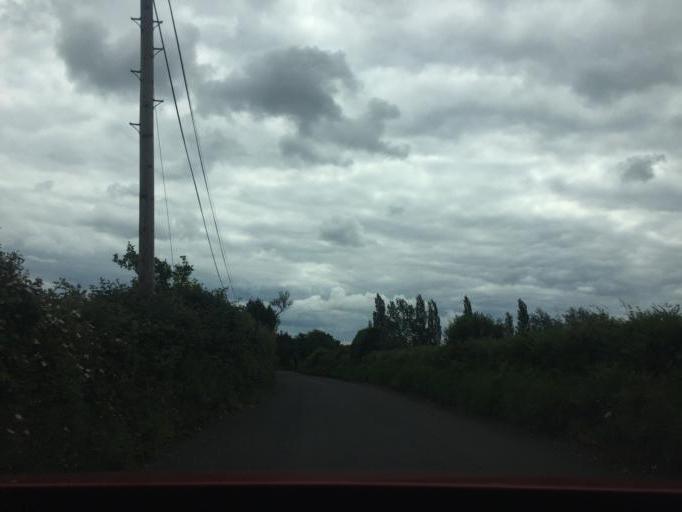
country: GB
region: England
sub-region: Hertfordshire
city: Wheathampstead
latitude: 51.8520
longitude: -0.3146
